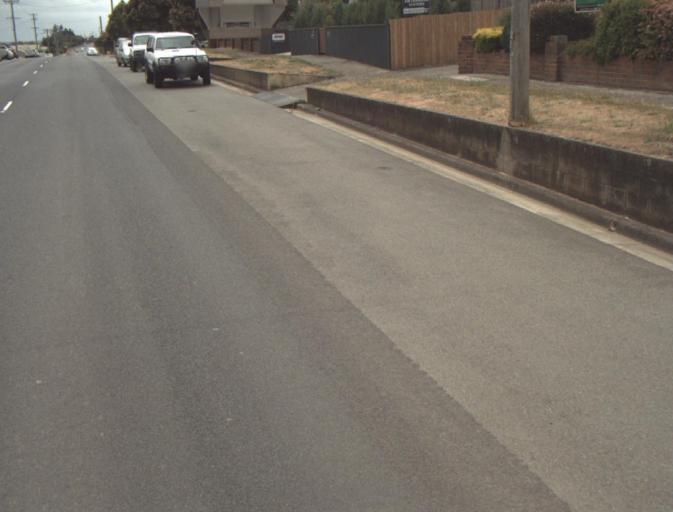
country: AU
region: Tasmania
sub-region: Launceston
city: Newstead
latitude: -41.4502
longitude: 147.1900
